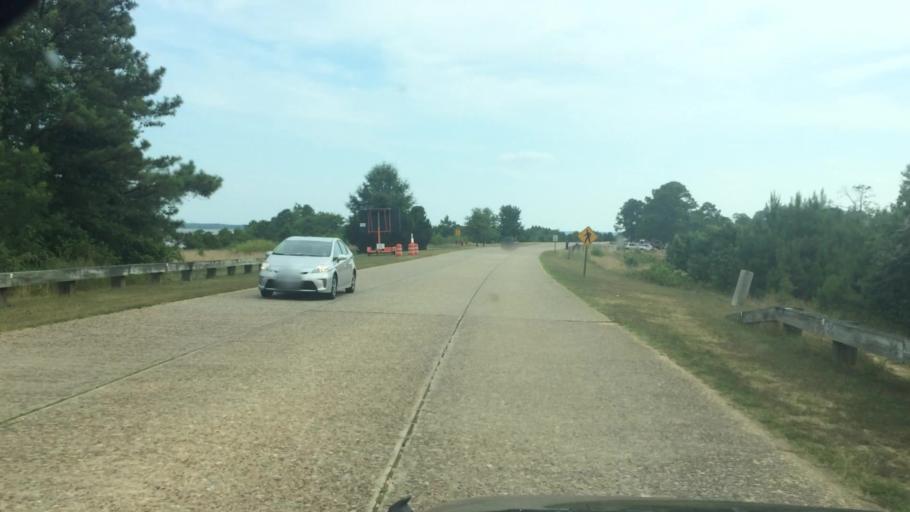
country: US
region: Virginia
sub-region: City of Williamsburg
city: Williamsburg
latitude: 37.2259
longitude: -76.6948
